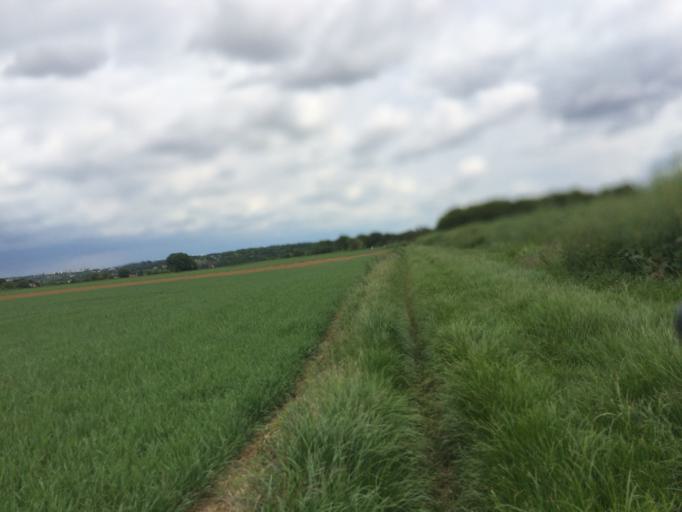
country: FR
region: Ile-de-France
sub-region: Departement de l'Essonne
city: Ballainvilliers
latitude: 48.6692
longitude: 2.3015
